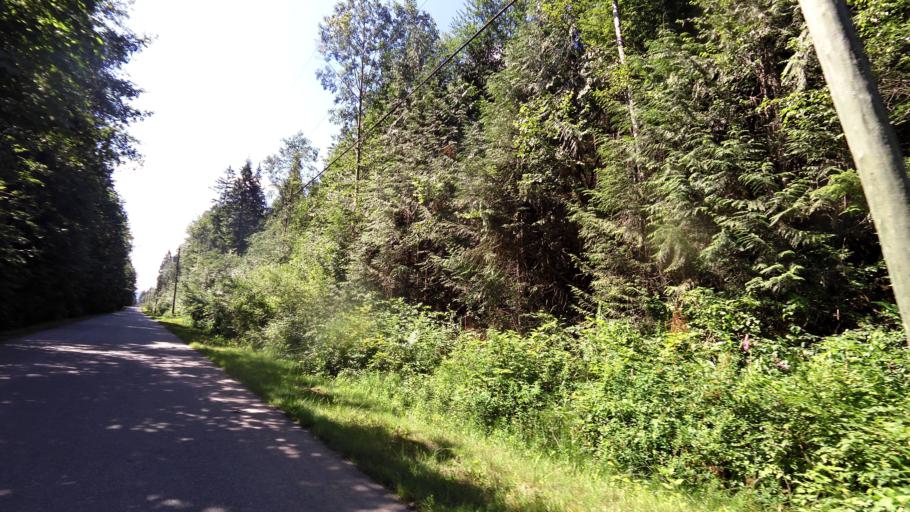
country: CA
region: British Columbia
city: Aldergrove
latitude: 49.2402
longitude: -122.3691
